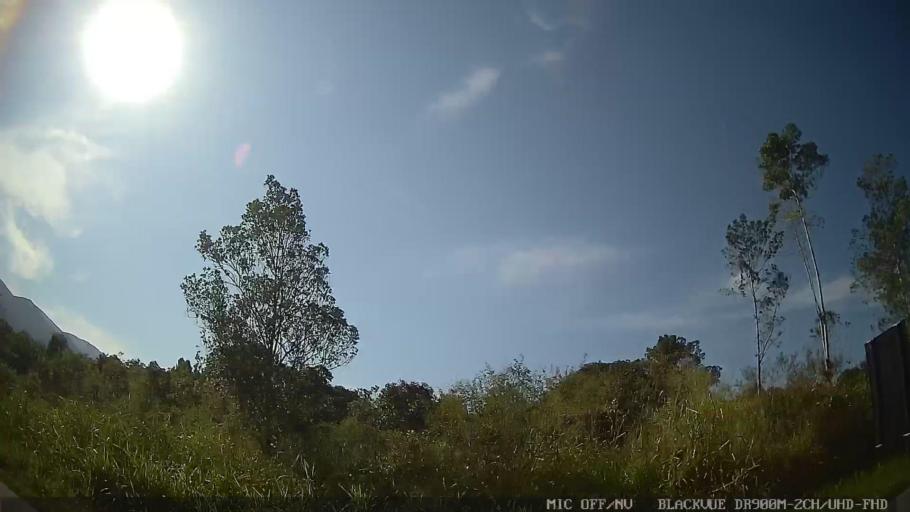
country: BR
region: Sao Paulo
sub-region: Santos
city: Santos
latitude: -23.8969
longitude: -46.2752
